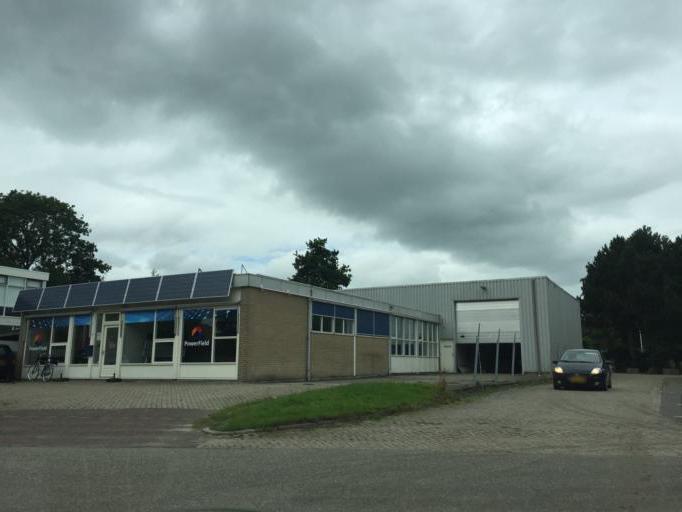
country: NL
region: Friesland
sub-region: Gemeente Dongeradeel
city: Dokkum
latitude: 53.3244
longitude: 6.0081
